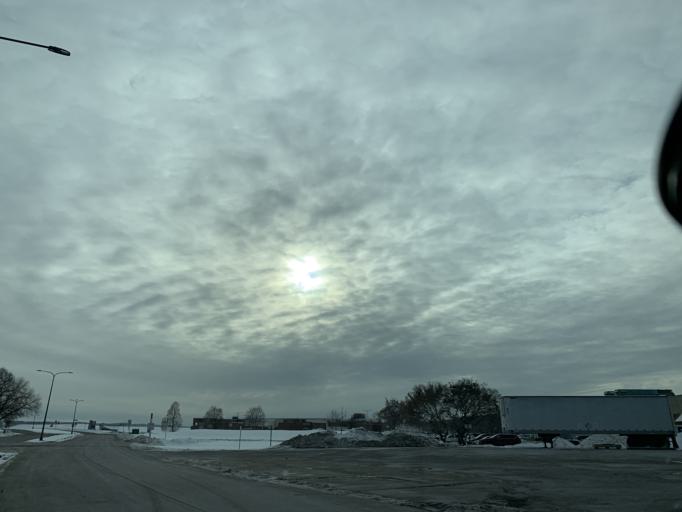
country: US
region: Minnesota
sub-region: Ramsey County
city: Saint Paul
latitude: 44.9435
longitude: -93.0737
